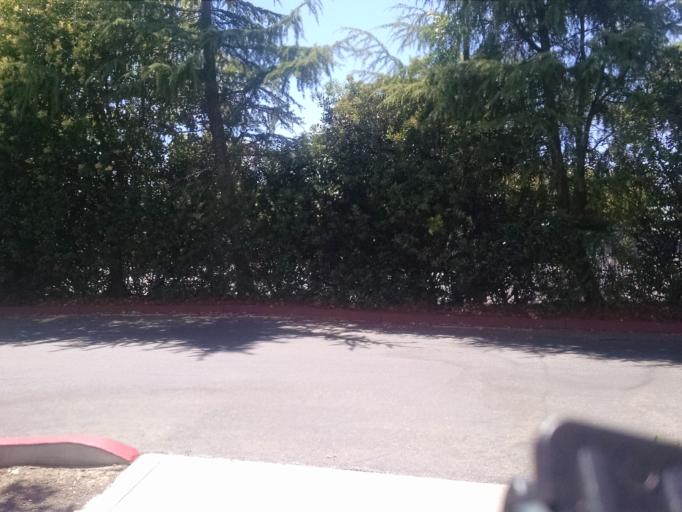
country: US
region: California
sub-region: Yolo County
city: Davis
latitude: 38.5490
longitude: -121.7173
